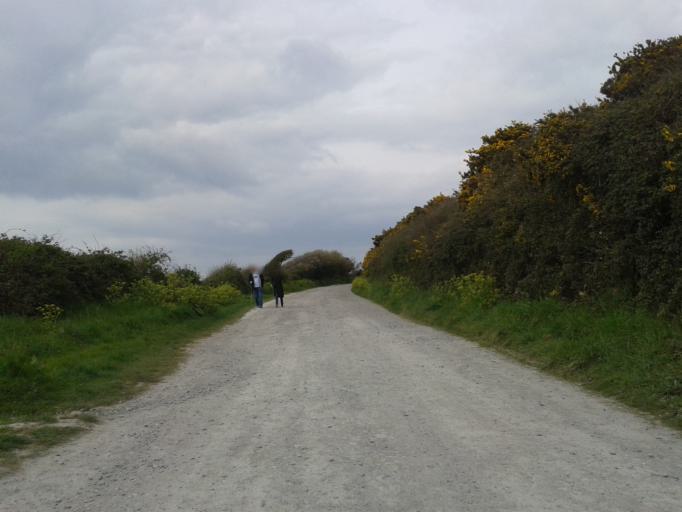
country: GB
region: England
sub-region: Devon
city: Braunton
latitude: 51.1575
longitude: -4.2106
